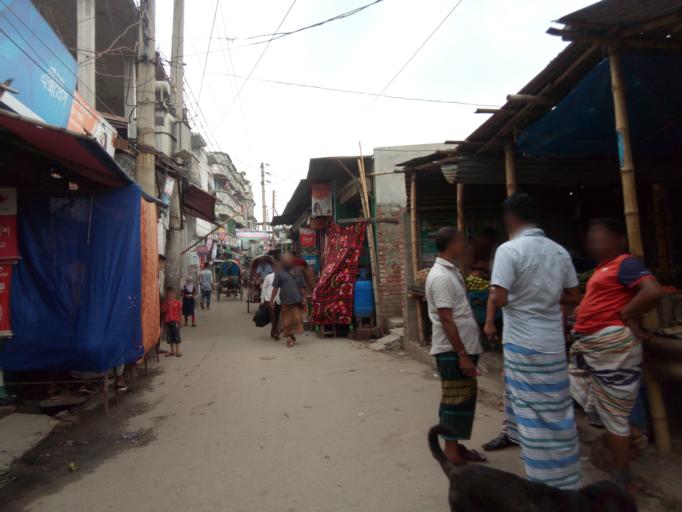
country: BD
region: Dhaka
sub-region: Dhaka
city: Dhaka
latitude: 23.6852
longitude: 90.4454
